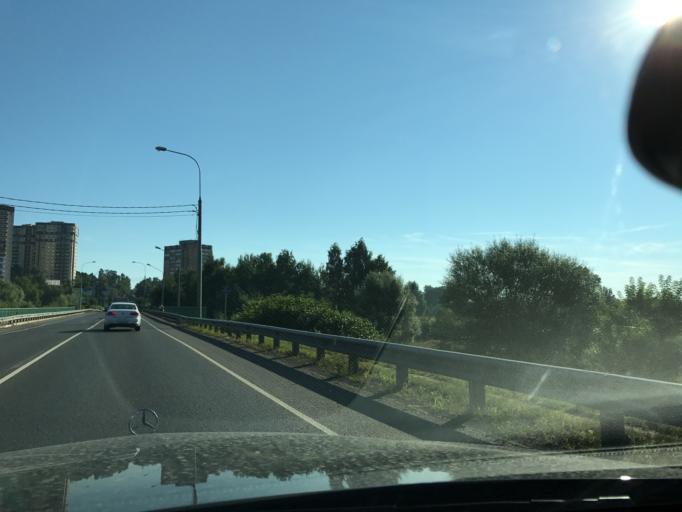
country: RU
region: Moskovskaya
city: Chkalovskiy
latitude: 55.9111
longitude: 38.1071
